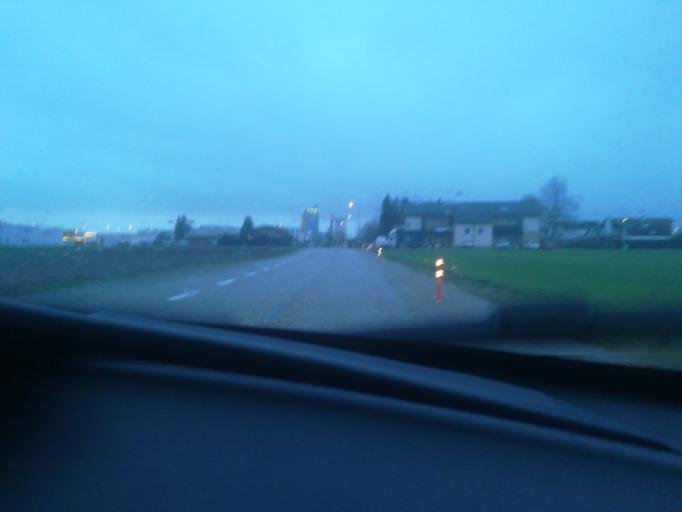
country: AT
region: Upper Austria
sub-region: Politischer Bezirk Perg
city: Perg
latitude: 48.2406
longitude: 14.6293
